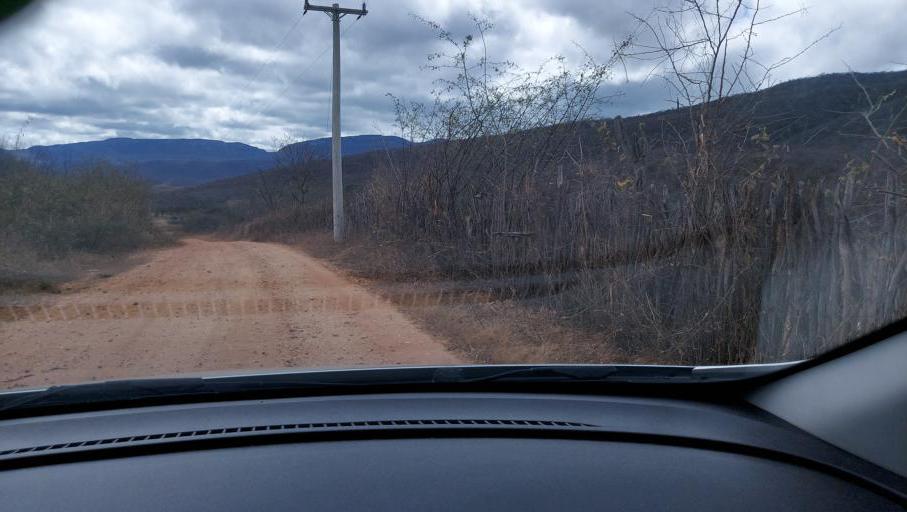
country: BR
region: Bahia
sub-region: Oliveira Dos Brejinhos
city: Beira Rio
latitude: -12.0736
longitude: -42.5408
